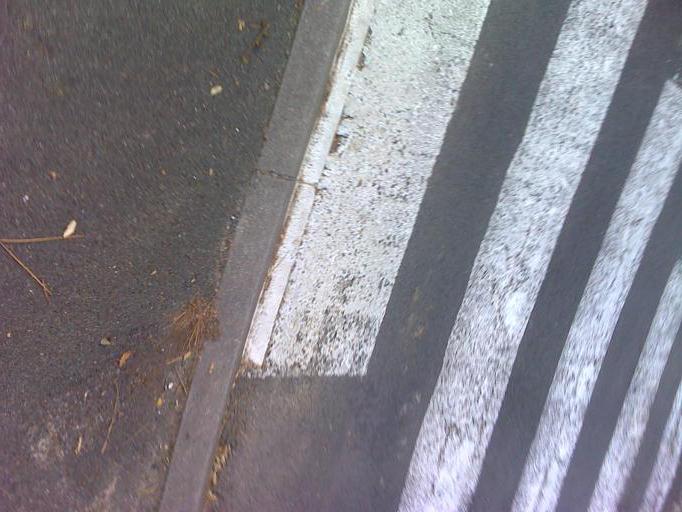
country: FR
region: Poitou-Charentes
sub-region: Departement de la Charente-Maritime
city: Saint-Palais-sur-Mer
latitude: 45.6445
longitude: -1.0931
